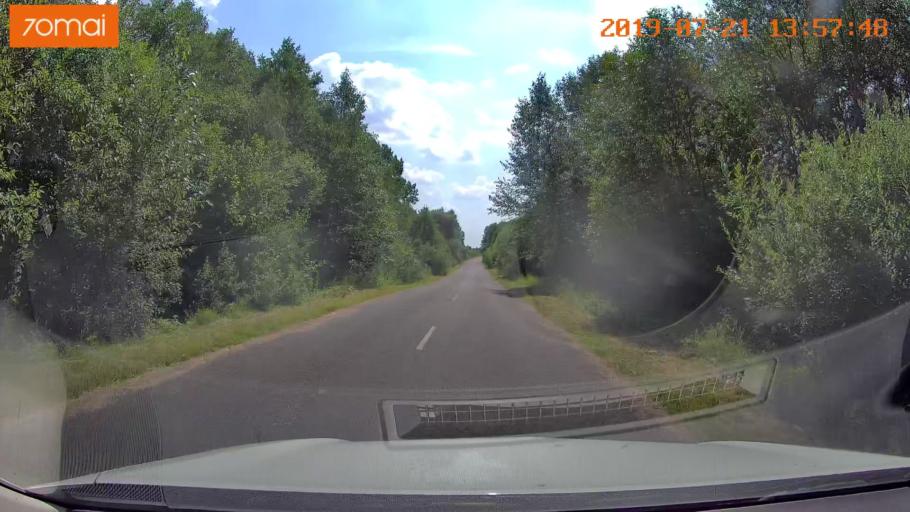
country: BY
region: Grodnenskaya
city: Lyubcha
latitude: 53.7681
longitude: 26.0869
